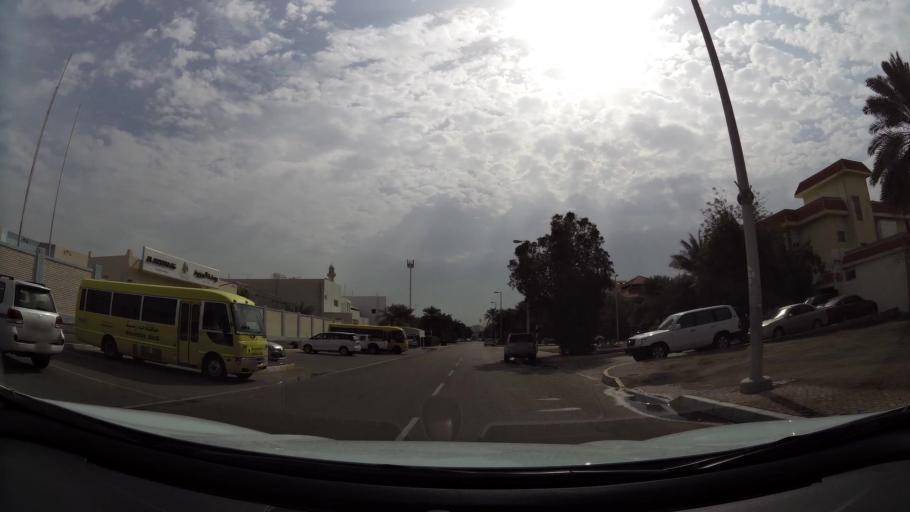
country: AE
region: Abu Dhabi
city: Abu Dhabi
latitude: 24.4427
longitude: 54.4141
